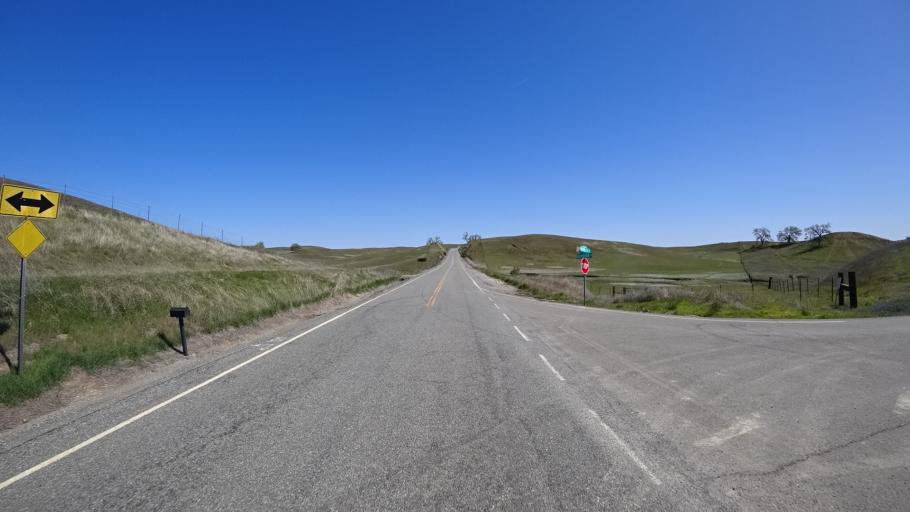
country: US
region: California
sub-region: Tehama County
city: Rancho Tehama Reserve
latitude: 39.8246
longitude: -122.3771
